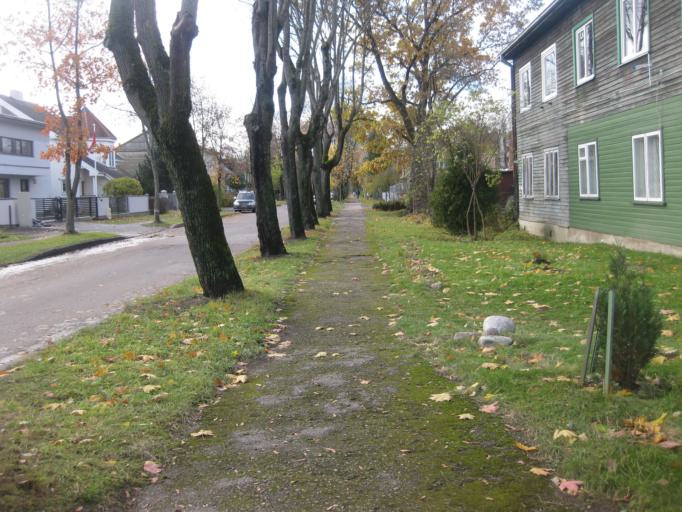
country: LT
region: Kauno apskritis
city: Dainava (Kaunas)
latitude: 54.9066
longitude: 23.9445
